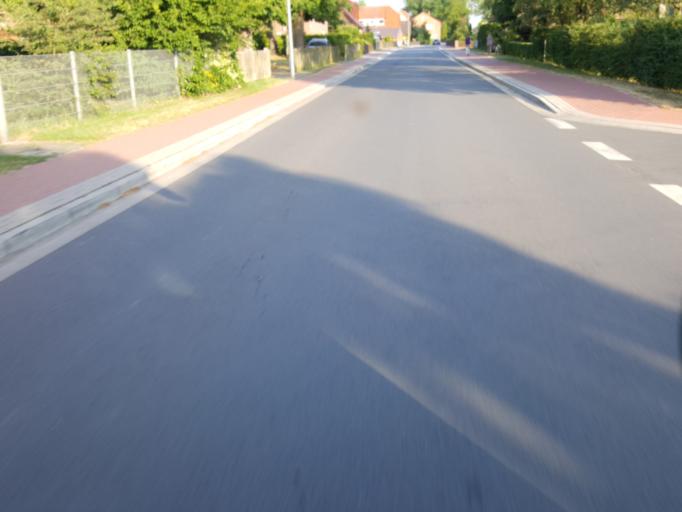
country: DE
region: Lower Saxony
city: Landesbergen
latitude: 52.5526
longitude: 9.1254
